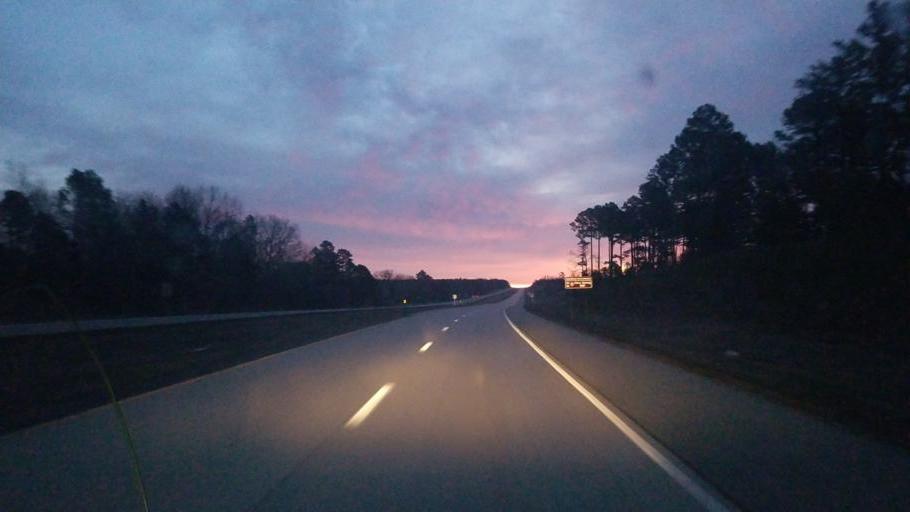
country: US
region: Missouri
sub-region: Shannon County
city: Winona
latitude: 36.9991
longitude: -91.4251
